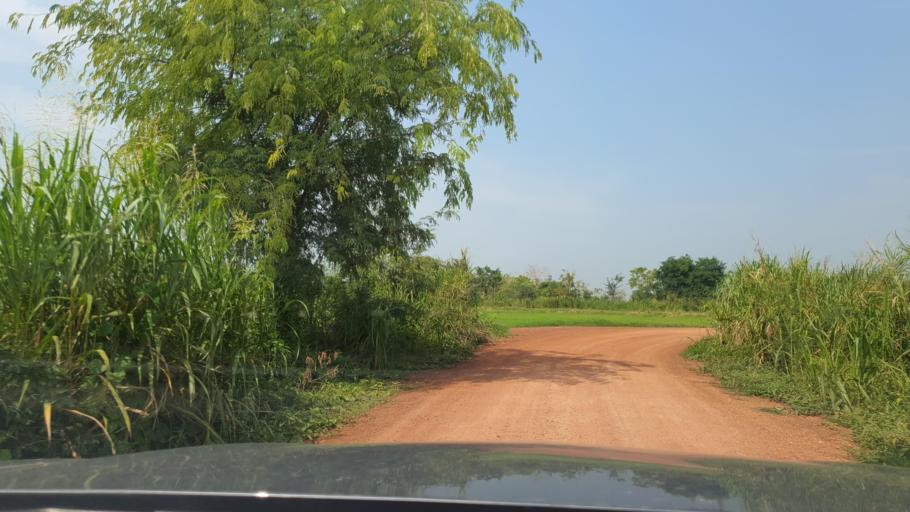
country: TH
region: Phitsanulok
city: Bang Rakam
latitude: 16.7986
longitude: 100.1083
